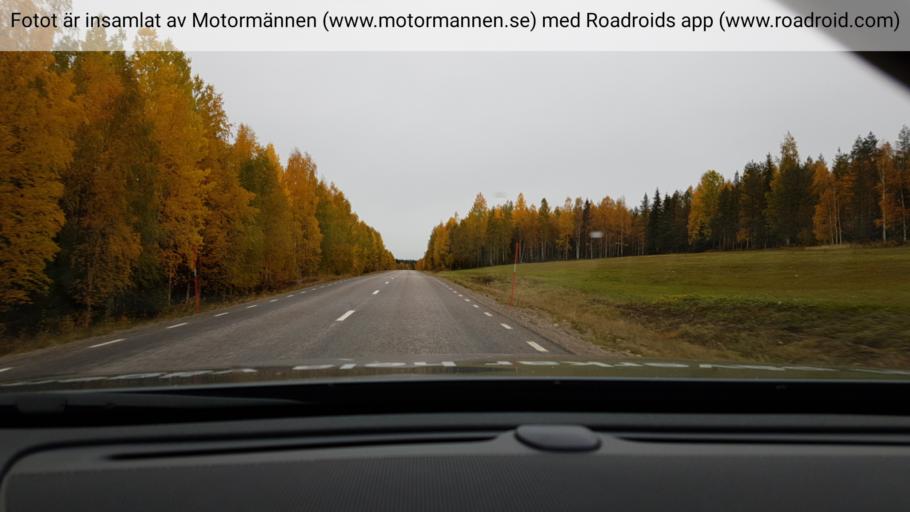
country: SE
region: Norrbotten
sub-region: Overkalix Kommun
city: OEverkalix
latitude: 66.5802
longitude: 22.7584
